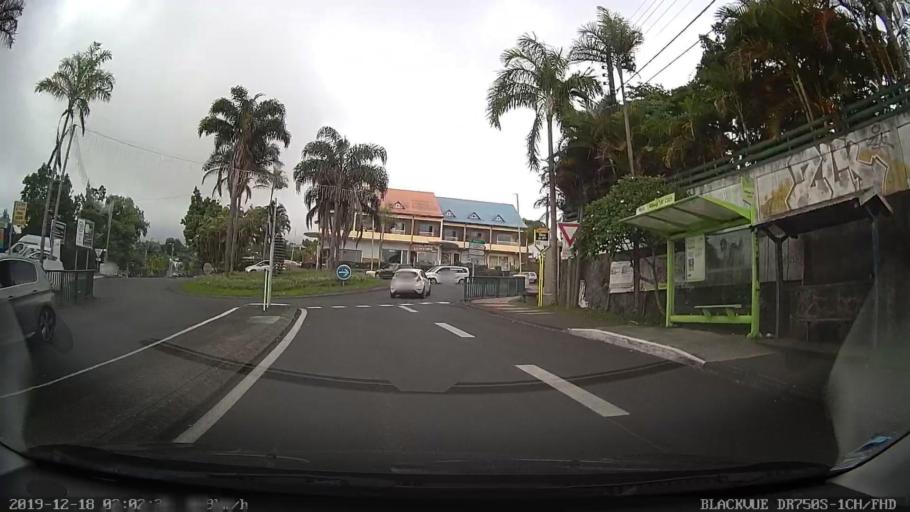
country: RE
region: Reunion
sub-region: Reunion
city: Le Tampon
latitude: -21.2508
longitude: 55.5214
